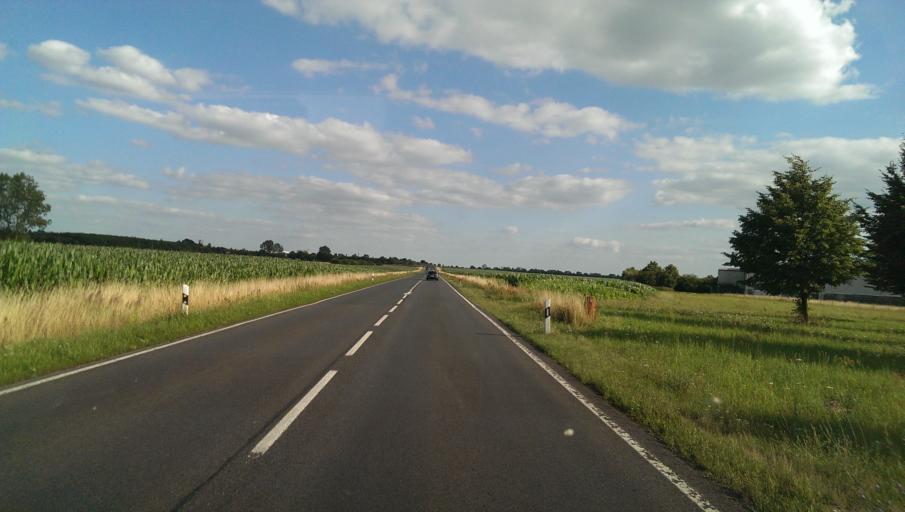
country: DE
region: Saxony
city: Rackwitz
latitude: 51.4298
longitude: 12.3708
